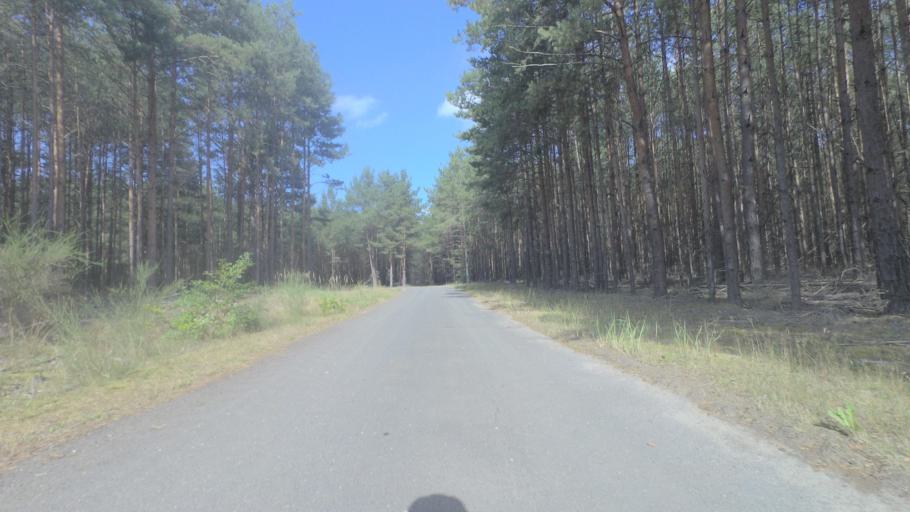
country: DE
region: Brandenburg
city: Munchehofe
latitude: 52.1763
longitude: 13.8736
